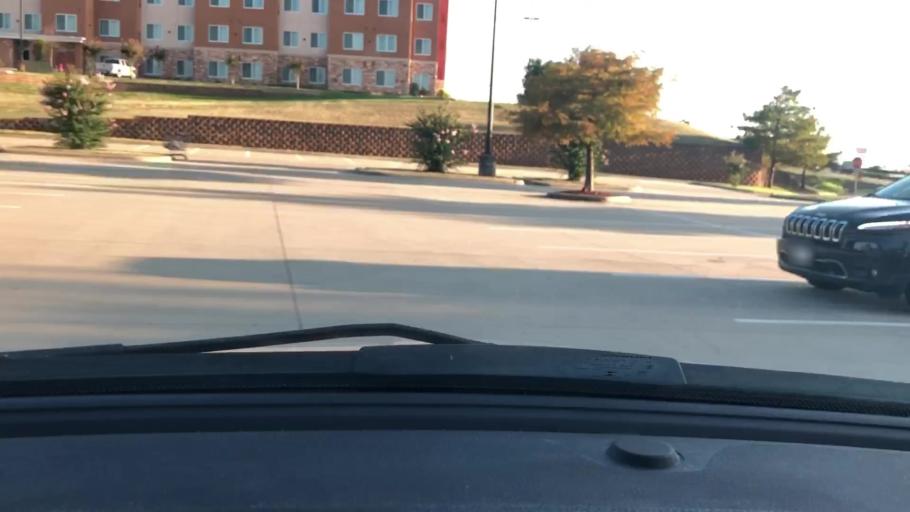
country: US
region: Texas
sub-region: Bowie County
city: Wake Village
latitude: 33.4577
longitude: -94.0904
